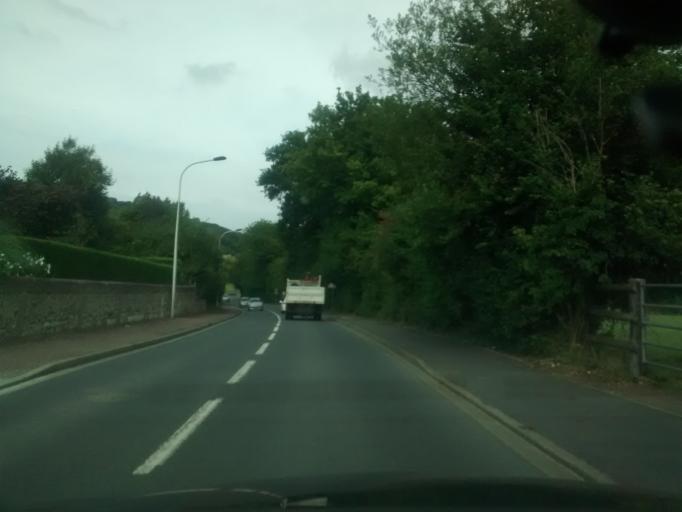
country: FR
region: Lower Normandy
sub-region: Departement du Calvados
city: Deauville
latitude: 49.3256
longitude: 0.0696
